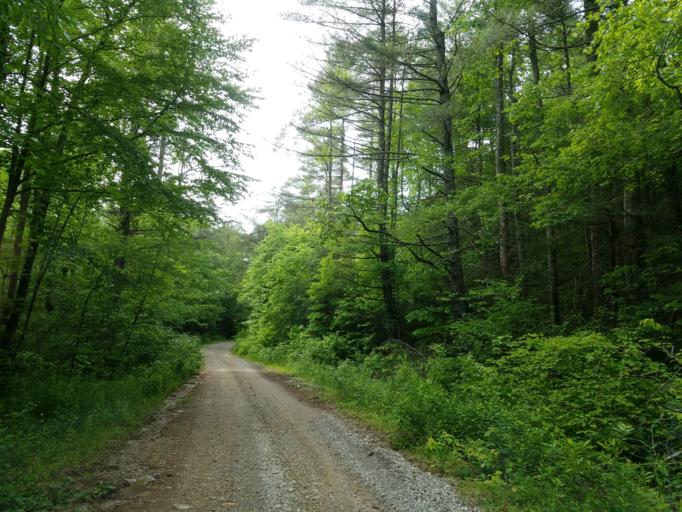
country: US
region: Georgia
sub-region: Union County
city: Blairsville
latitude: 34.7520
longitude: -83.9964
